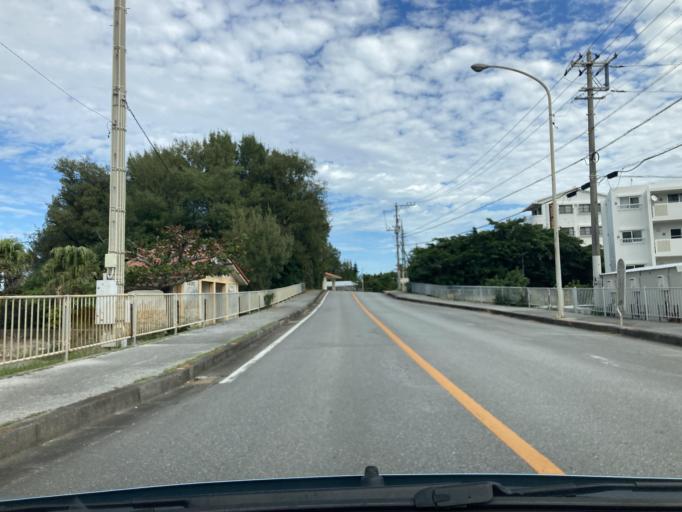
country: JP
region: Okinawa
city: Ishikawa
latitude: 26.4236
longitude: 127.7453
